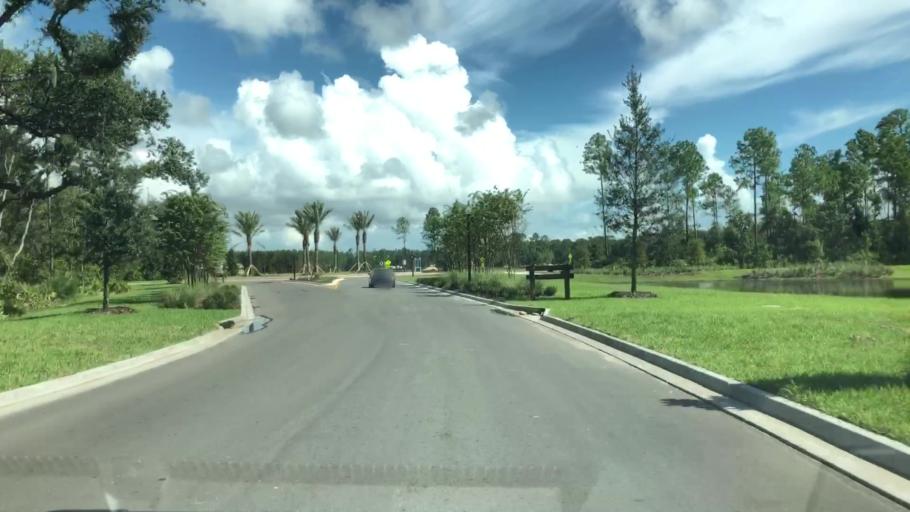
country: US
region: Florida
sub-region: Saint Johns County
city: Palm Valley
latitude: 30.1358
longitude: -81.4039
